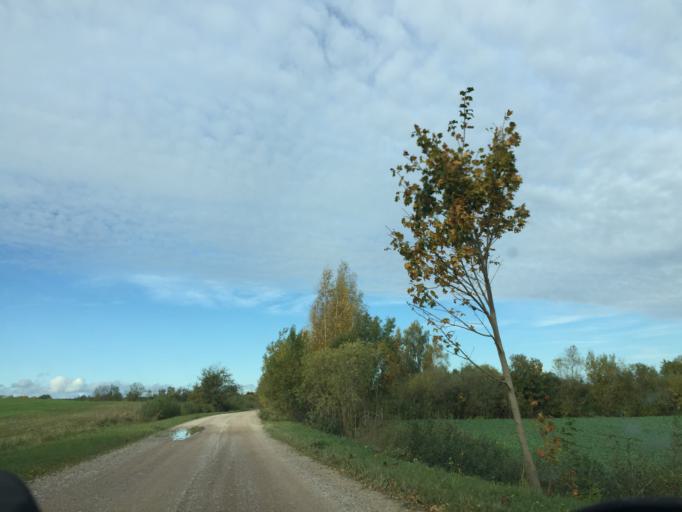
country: LV
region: Jaunpils
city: Jaunpils
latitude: 56.6196
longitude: 23.0664
